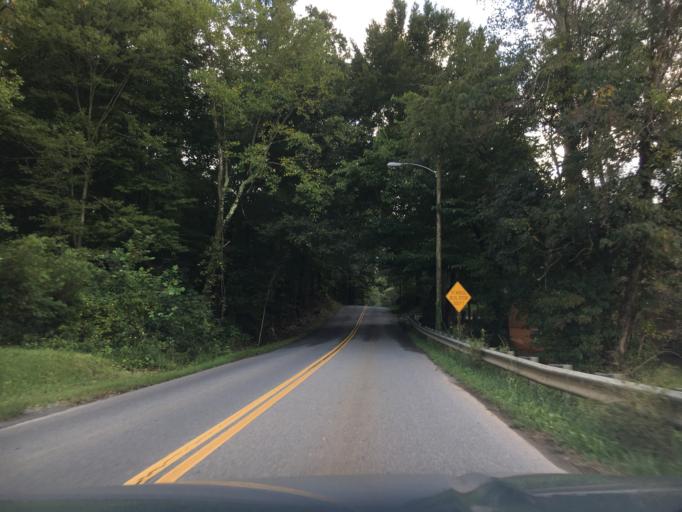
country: US
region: Virginia
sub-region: City of Lynchburg
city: Lynchburg
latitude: 37.3781
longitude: -79.1457
